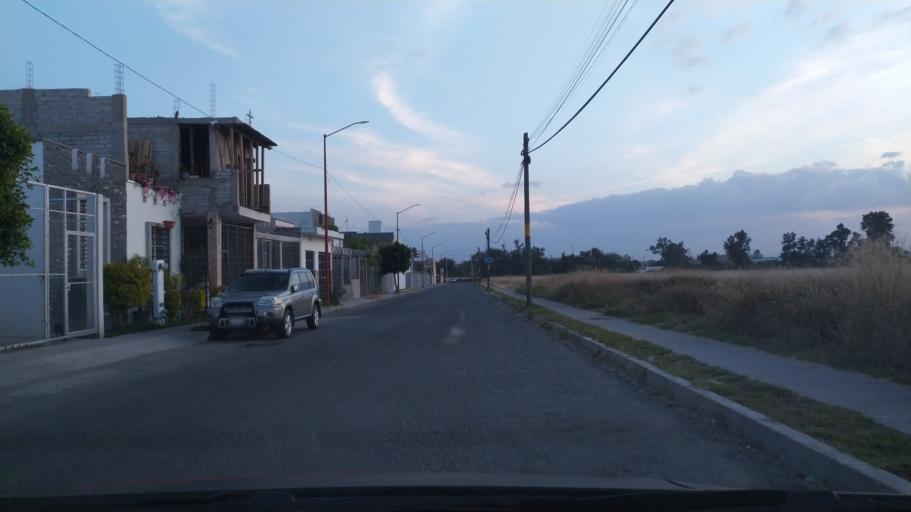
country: MX
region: Guanajuato
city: San Francisco del Rincon
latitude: 21.0353
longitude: -101.8486
